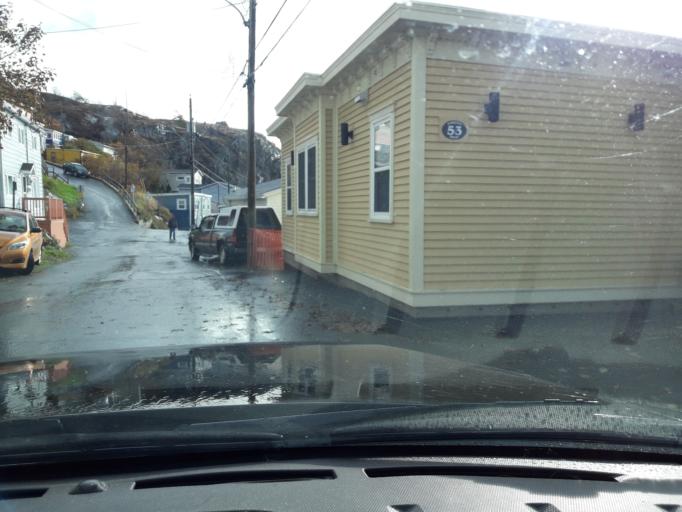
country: CA
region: Newfoundland and Labrador
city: St. John's
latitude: 47.5702
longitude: -52.6929
